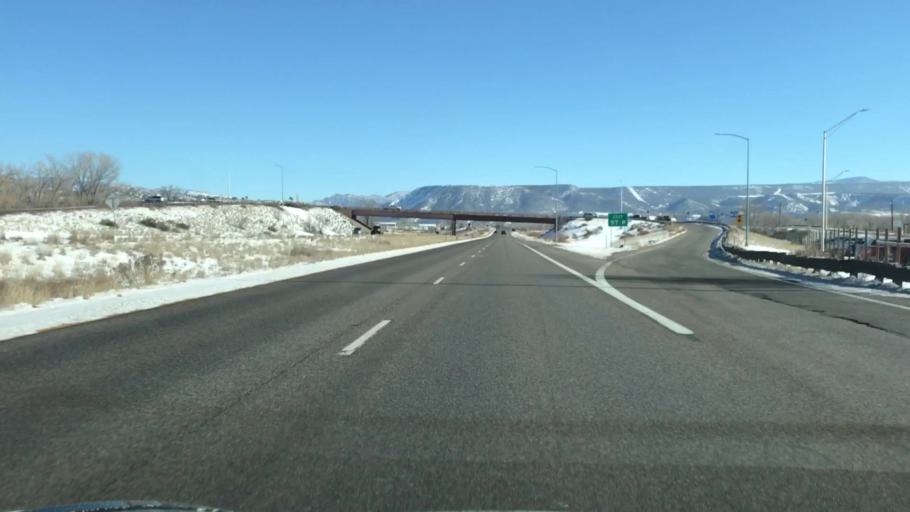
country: US
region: Colorado
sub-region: Garfield County
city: Silt
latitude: 39.5451
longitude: -107.6566
